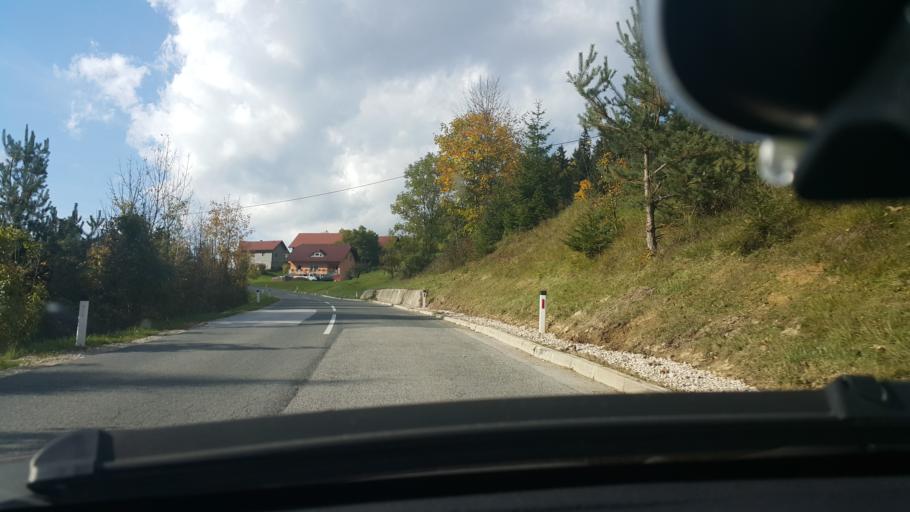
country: SI
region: Zrece
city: Zrece
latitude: 46.3753
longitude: 15.3377
